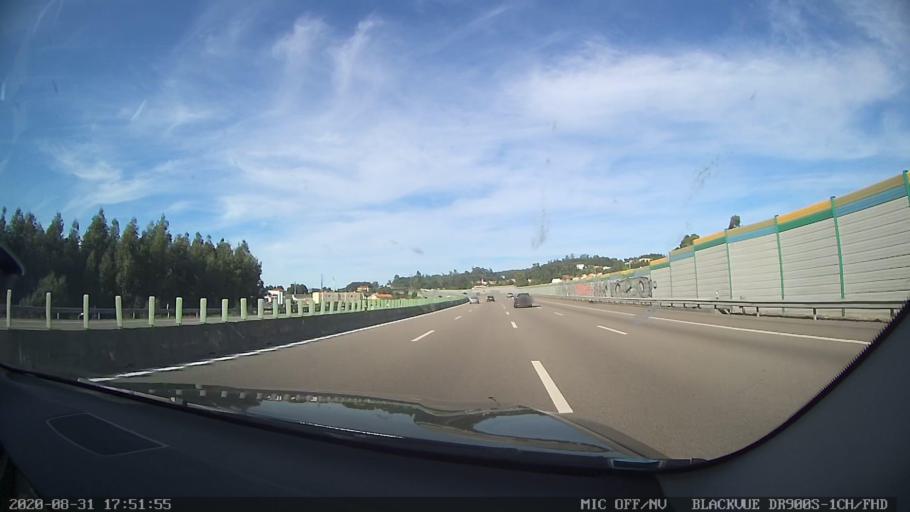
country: PT
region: Porto
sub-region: Vila Nova de Gaia
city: Grijo
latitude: 41.0232
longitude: -8.5781
